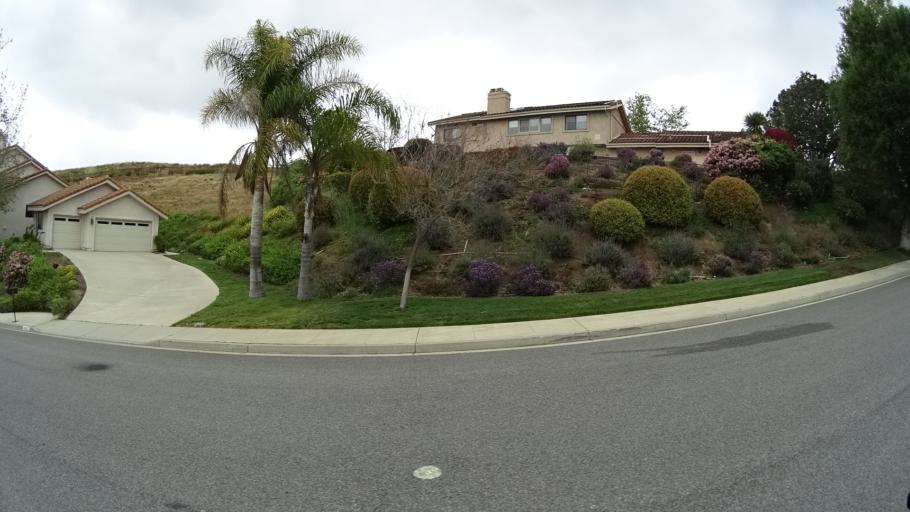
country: US
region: California
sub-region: Ventura County
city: Moorpark
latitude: 34.2293
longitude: -118.8921
